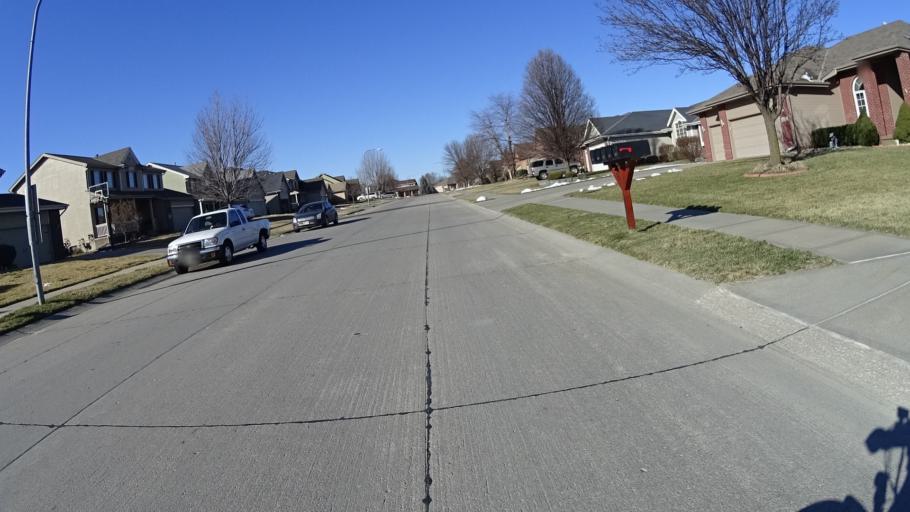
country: US
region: Nebraska
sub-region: Sarpy County
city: Papillion
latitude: 41.1563
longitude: -96.0029
